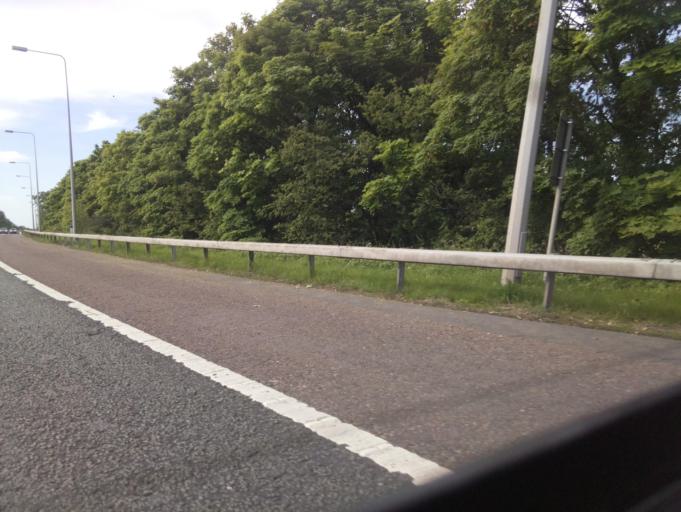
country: GB
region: England
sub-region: Lancashire
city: Clayton-le-Woods
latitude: 53.7318
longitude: -2.6437
